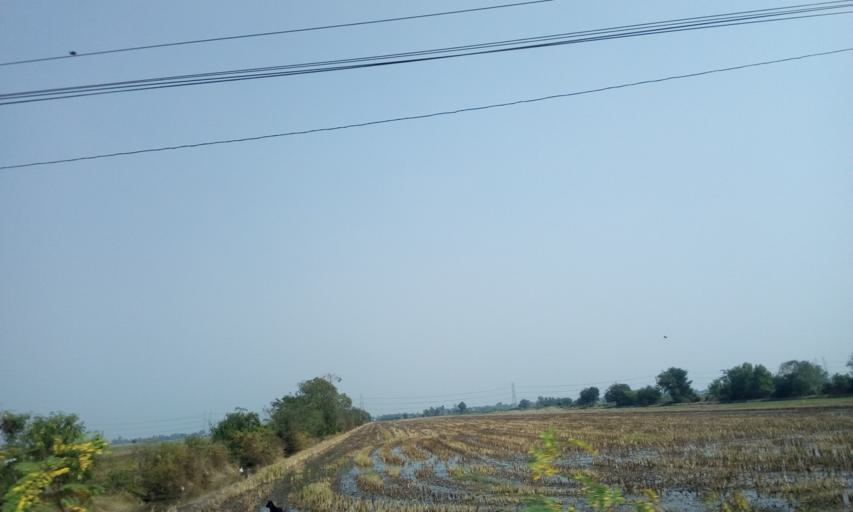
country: TH
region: Pathum Thani
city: Ban Rangsit
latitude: 14.0066
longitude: 100.7569
